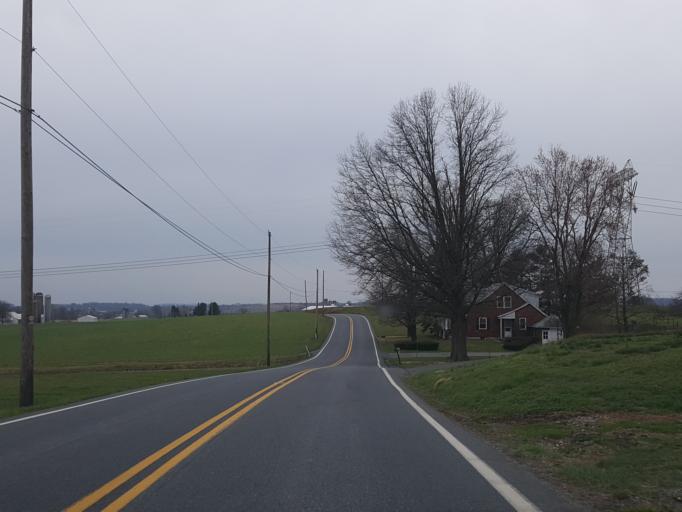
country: US
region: Pennsylvania
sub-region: Lancaster County
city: Rheems
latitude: 40.2010
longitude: -76.5156
